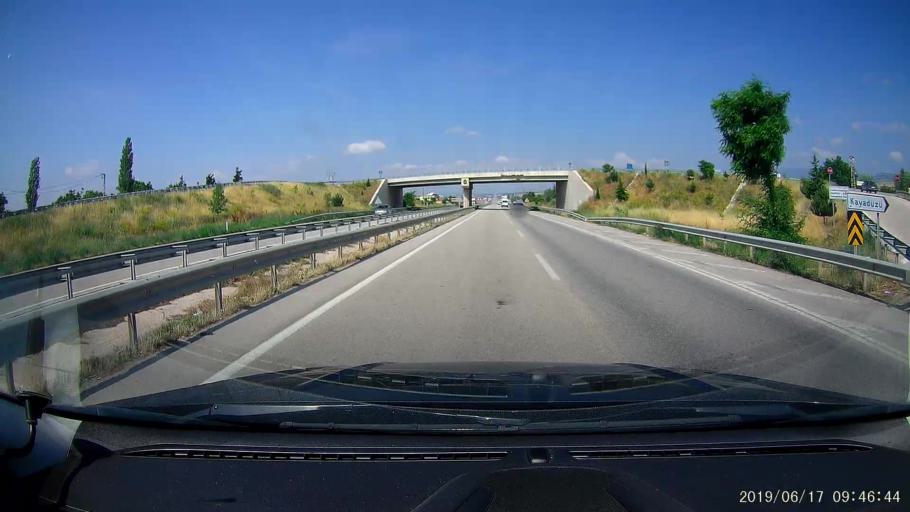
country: TR
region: Amasya
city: Suluova
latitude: 40.8779
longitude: 35.5956
